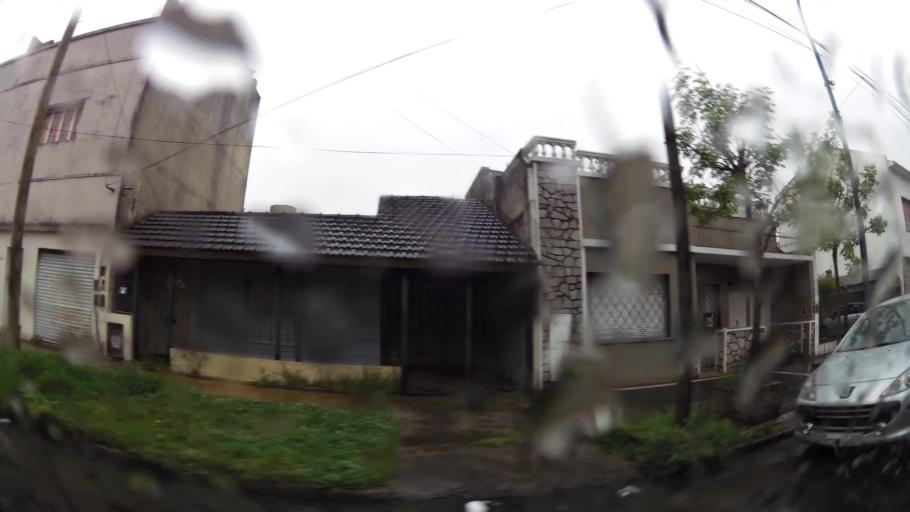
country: AR
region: Buenos Aires
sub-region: Partido de Lanus
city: Lanus
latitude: -34.7161
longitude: -58.4046
